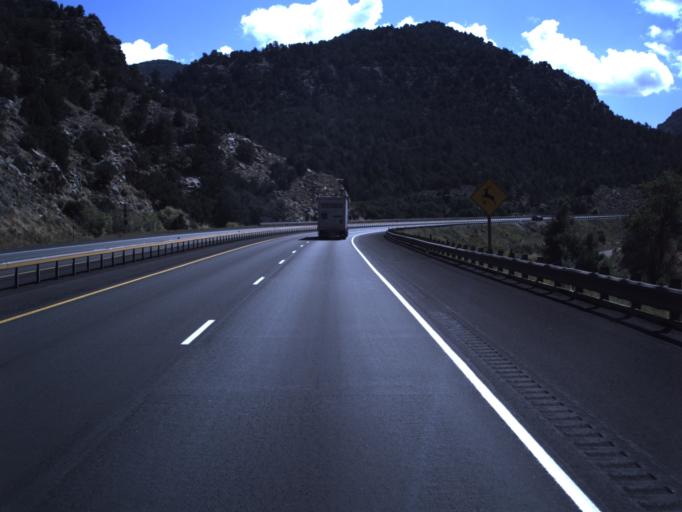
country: US
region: Utah
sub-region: Sevier County
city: Salina
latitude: 38.9048
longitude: -111.6363
